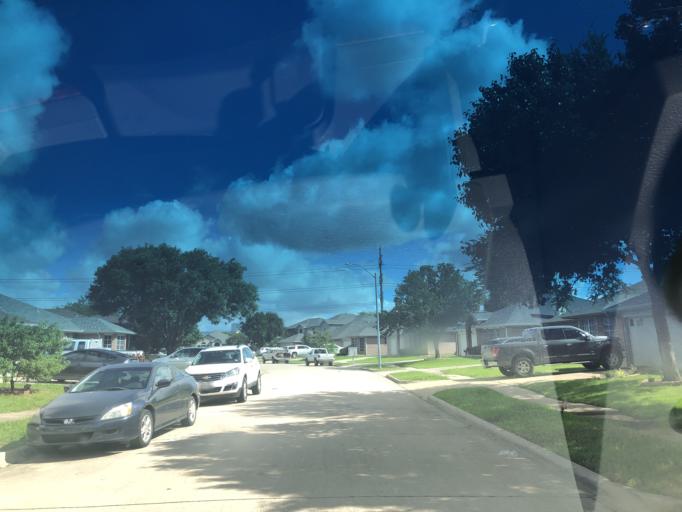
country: US
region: Texas
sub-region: Dallas County
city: Grand Prairie
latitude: 32.6968
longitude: -97.0307
